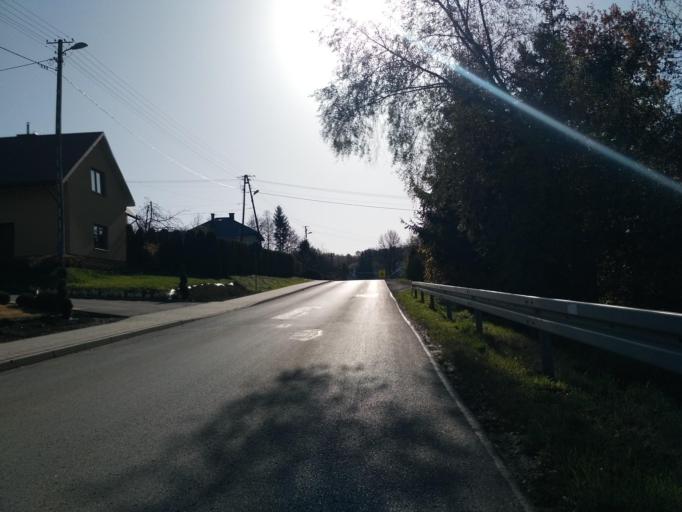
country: PL
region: Subcarpathian Voivodeship
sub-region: Powiat rzeszowski
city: Blazowa
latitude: 49.8581
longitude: 22.1315
